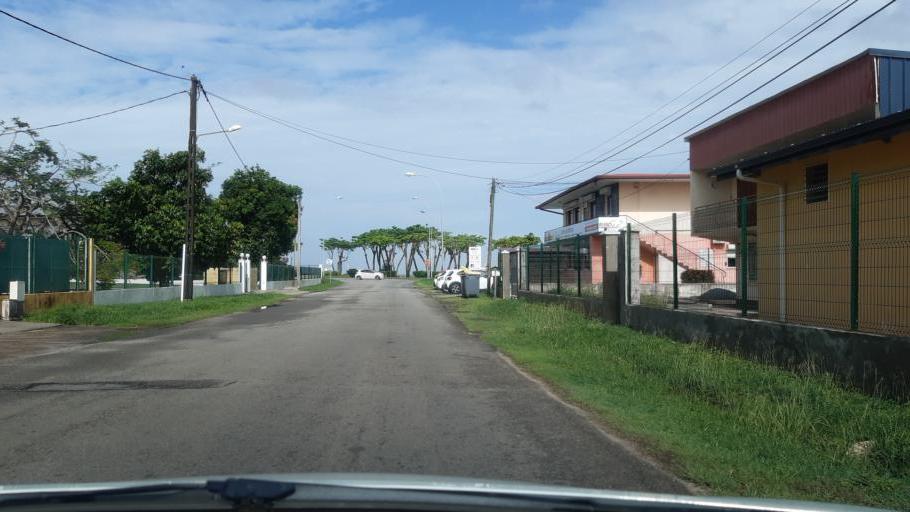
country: GF
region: Guyane
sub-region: Guyane
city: Cayenne
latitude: 4.9430
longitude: -52.3181
